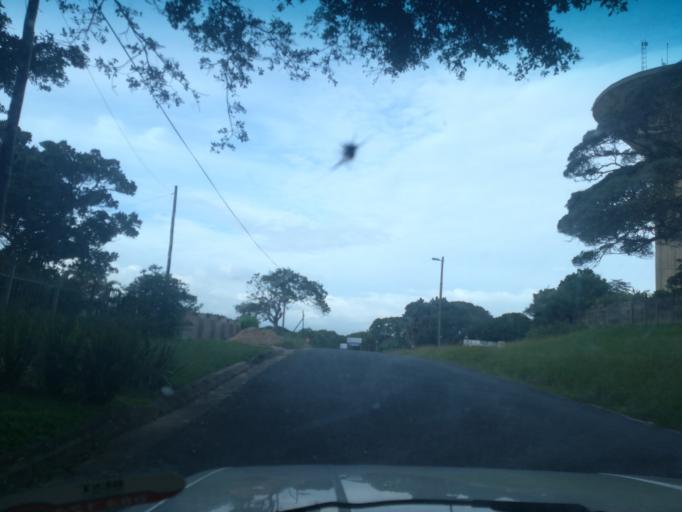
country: ZA
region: KwaZulu-Natal
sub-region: Ugu District Municipality
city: Scottburgh
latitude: -30.2889
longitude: 30.7488
